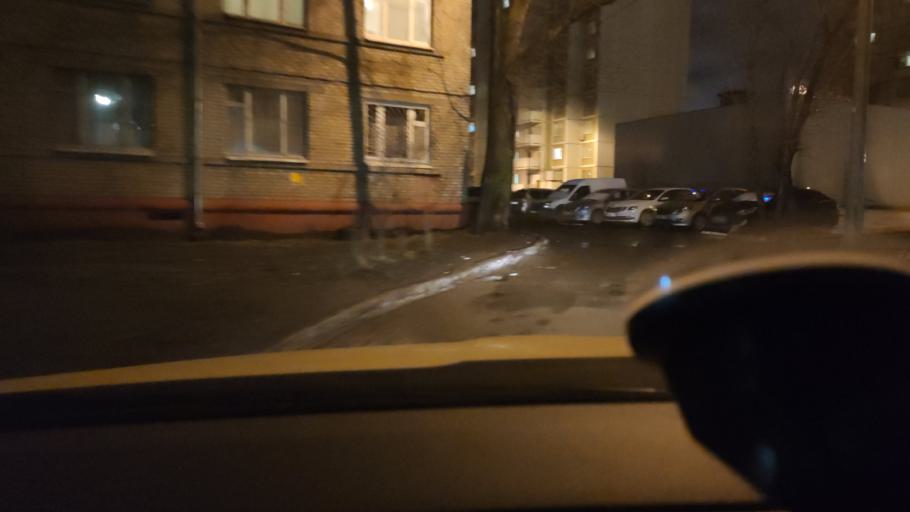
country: RU
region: Moscow
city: Metrogorodok
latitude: 55.8113
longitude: 37.7903
